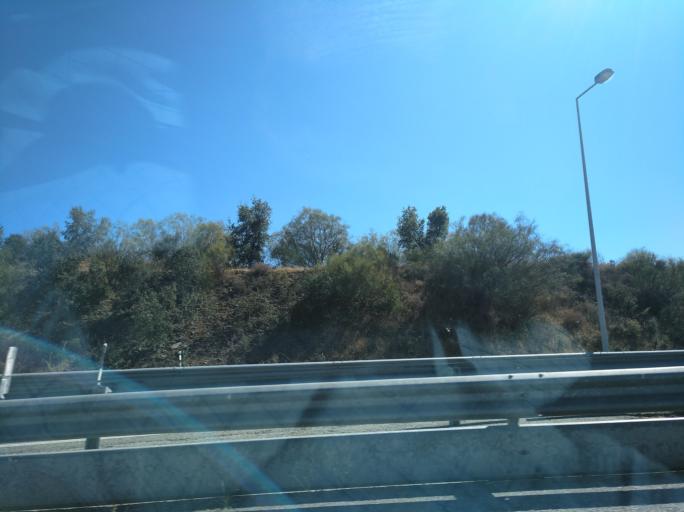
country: PT
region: Evora
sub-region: Estremoz
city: Estremoz
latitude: 38.8185
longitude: -7.6063
